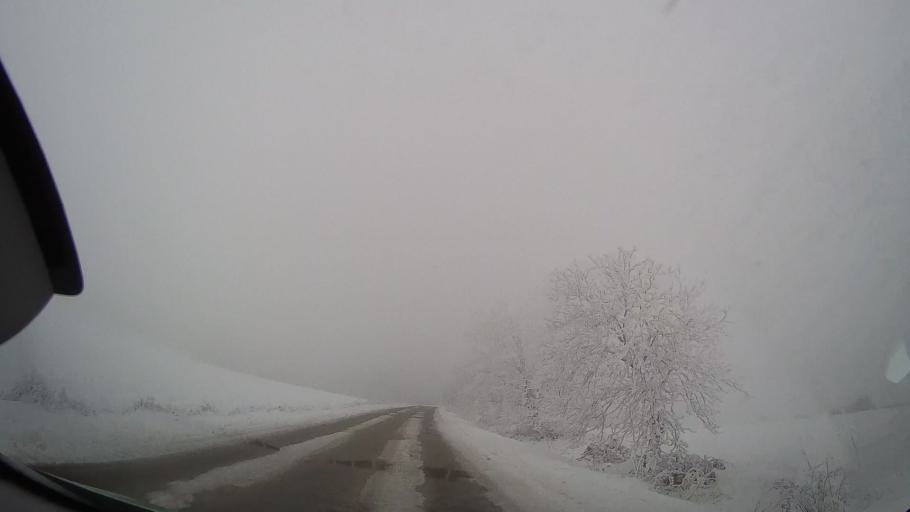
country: RO
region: Neamt
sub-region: Comuna Valea Ursului
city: Valea Ursului
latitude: 46.8345
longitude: 27.0711
